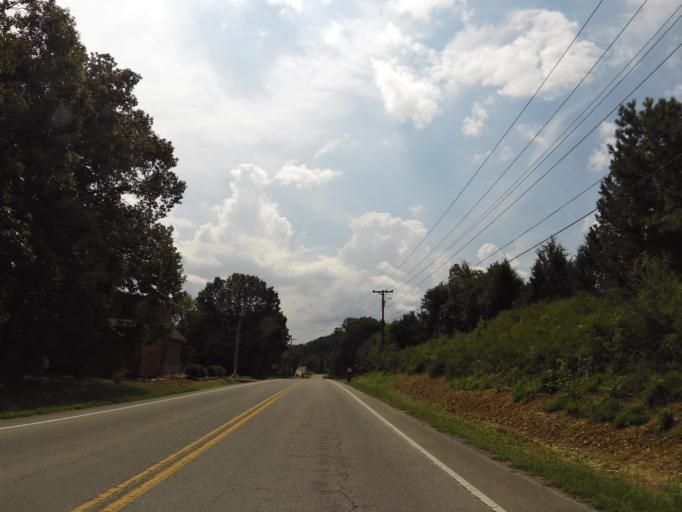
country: US
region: Tennessee
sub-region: Perry County
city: Linden
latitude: 35.7889
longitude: -87.7787
